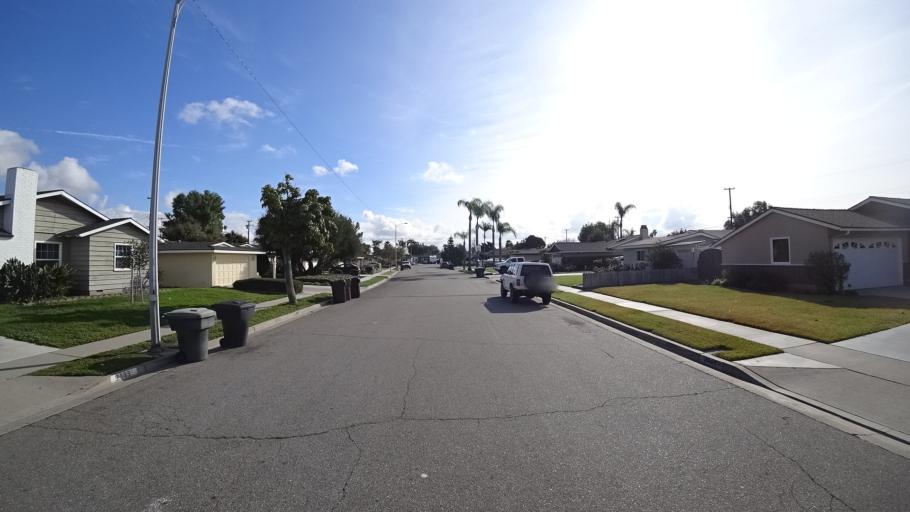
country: US
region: California
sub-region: Orange County
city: Stanton
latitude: 33.8258
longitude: -117.9701
